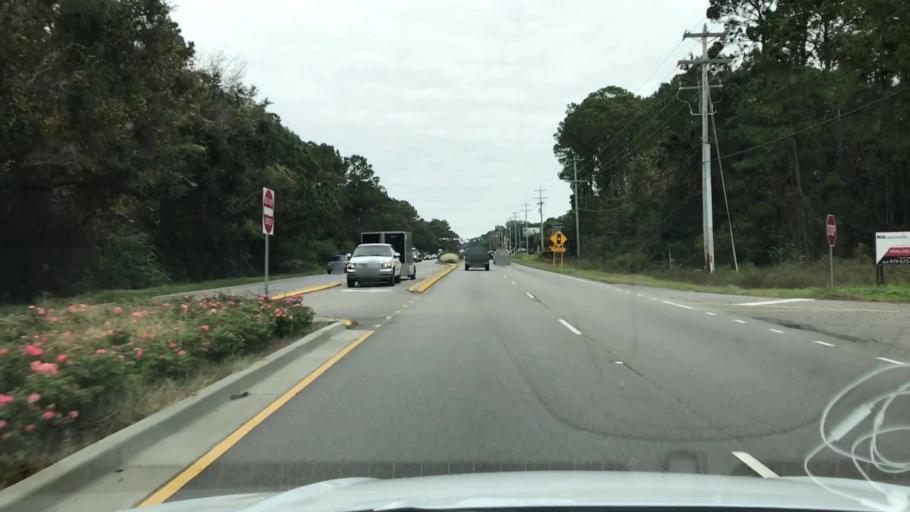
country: US
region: South Carolina
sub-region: Georgetown County
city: Murrells Inlet
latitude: 33.4546
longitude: -79.1161
